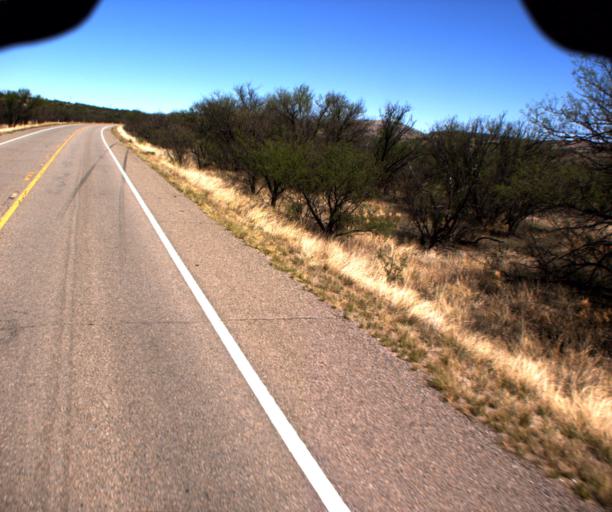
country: US
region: Arizona
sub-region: Santa Cruz County
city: Rio Rico
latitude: 31.6158
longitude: -110.7199
